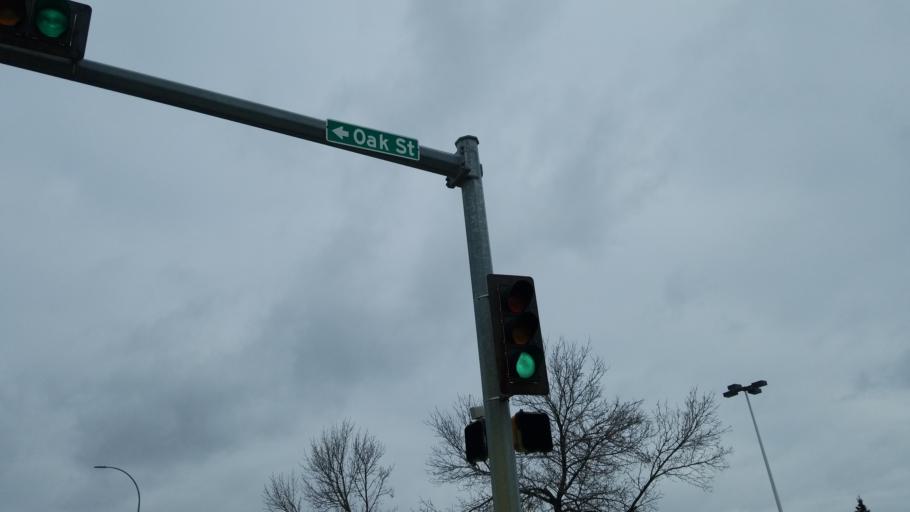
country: CA
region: Alberta
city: Sherwood Park
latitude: 53.5303
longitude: -113.2956
